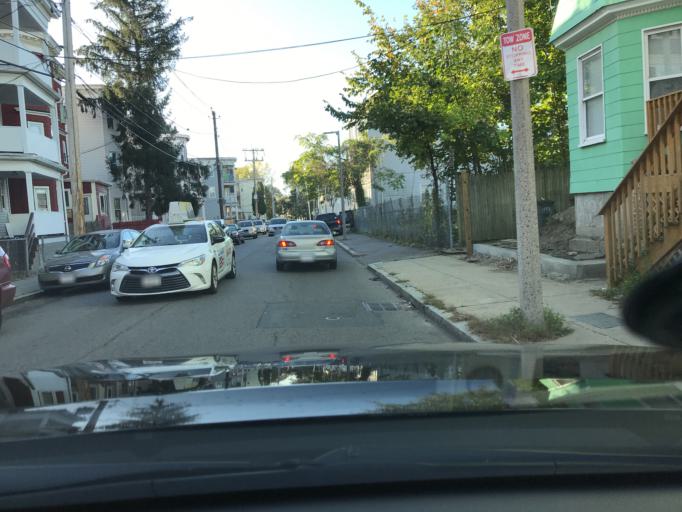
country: US
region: Massachusetts
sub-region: Suffolk County
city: Jamaica Plain
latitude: 42.2958
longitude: -71.0783
